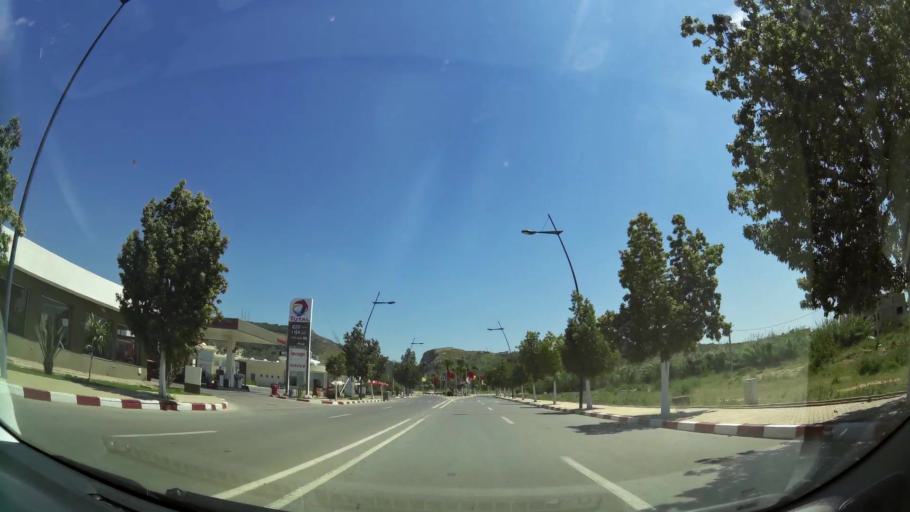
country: MA
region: Oriental
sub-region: Berkane-Taourirt
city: Madagh
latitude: 35.0688
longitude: -2.2167
